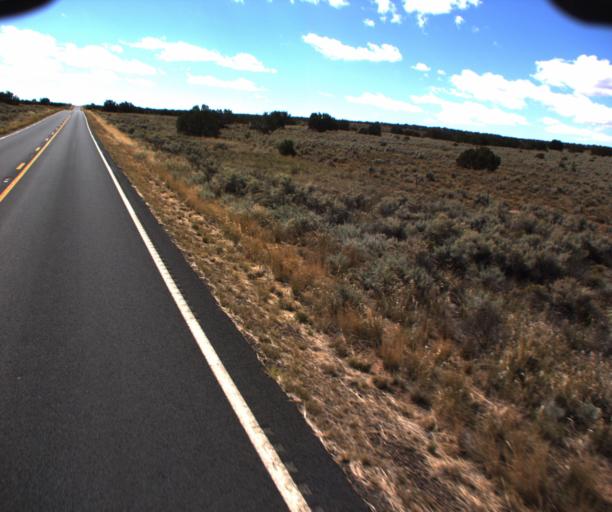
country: US
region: Arizona
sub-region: Apache County
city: Houck
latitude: 35.1638
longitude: -109.3373
